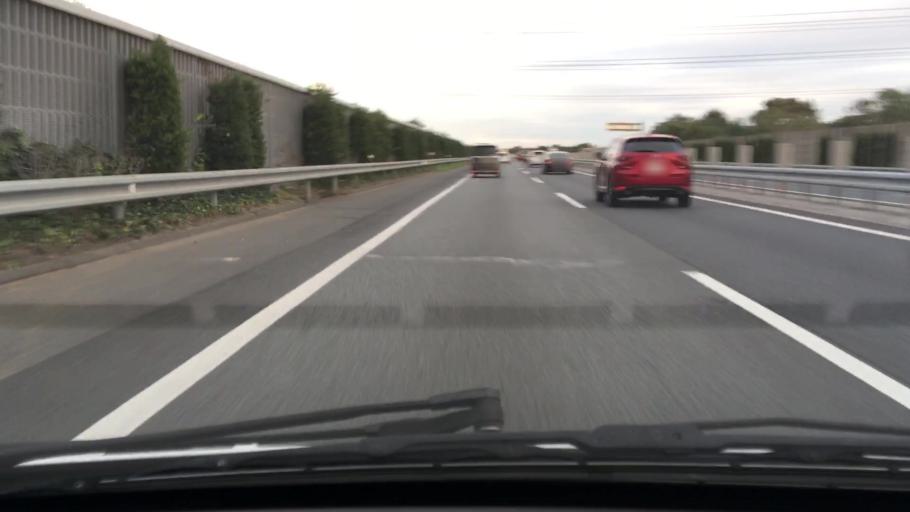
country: JP
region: Chiba
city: Ichihara
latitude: 35.5082
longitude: 140.1077
